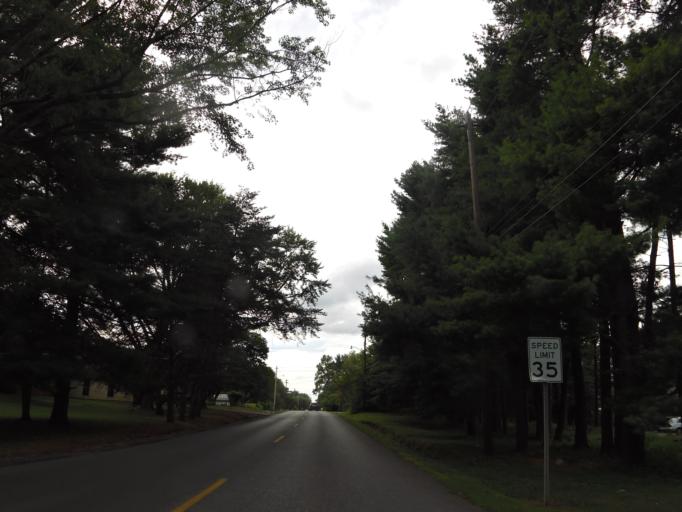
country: US
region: Kentucky
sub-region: Christian County
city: Hopkinsville
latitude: 36.8506
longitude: -87.5145
